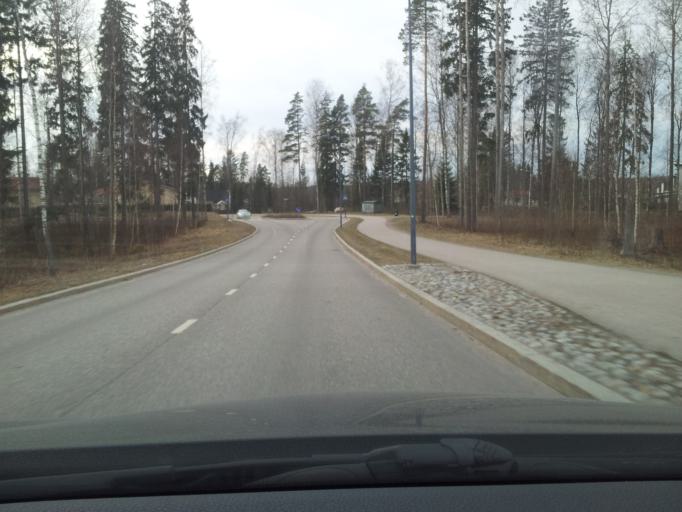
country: FI
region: Uusimaa
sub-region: Helsinki
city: Espoo
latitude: 60.1635
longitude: 24.6710
